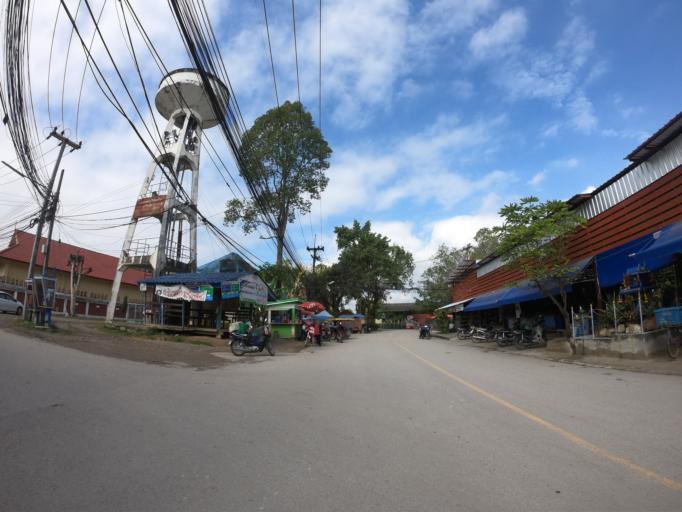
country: TH
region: Chiang Mai
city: San Sai
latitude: 18.8668
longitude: 99.0216
